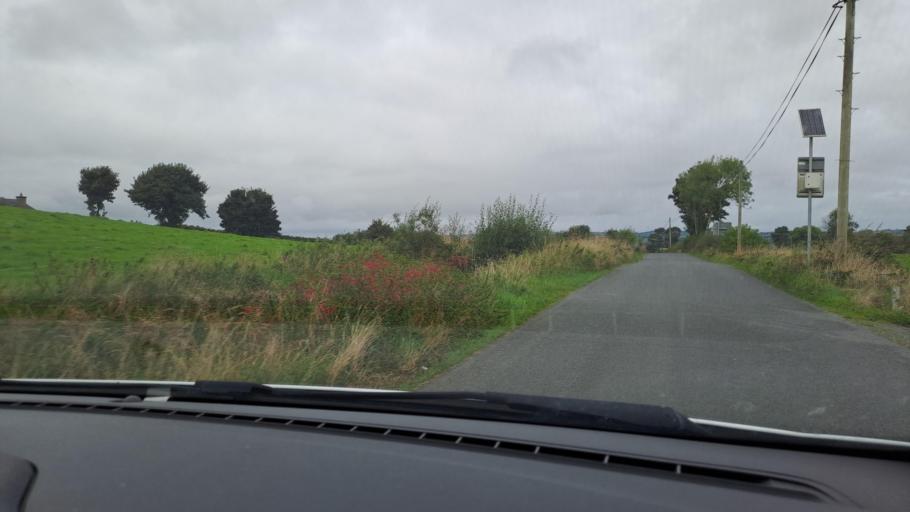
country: IE
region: Ulster
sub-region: An Cabhan
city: Kingscourt
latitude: 54.0147
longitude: -6.8223
